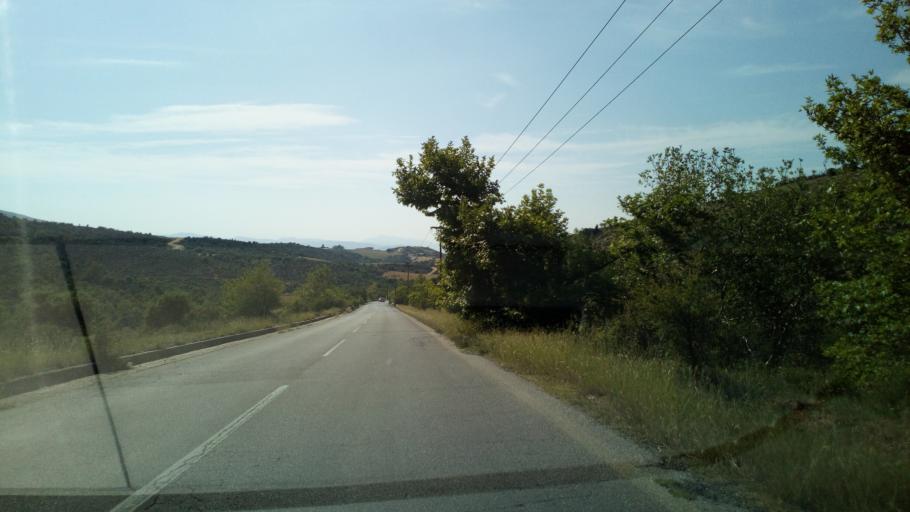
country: GR
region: Central Macedonia
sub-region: Nomos Chalkidikis
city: Arnaia
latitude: 40.5007
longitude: 23.4904
